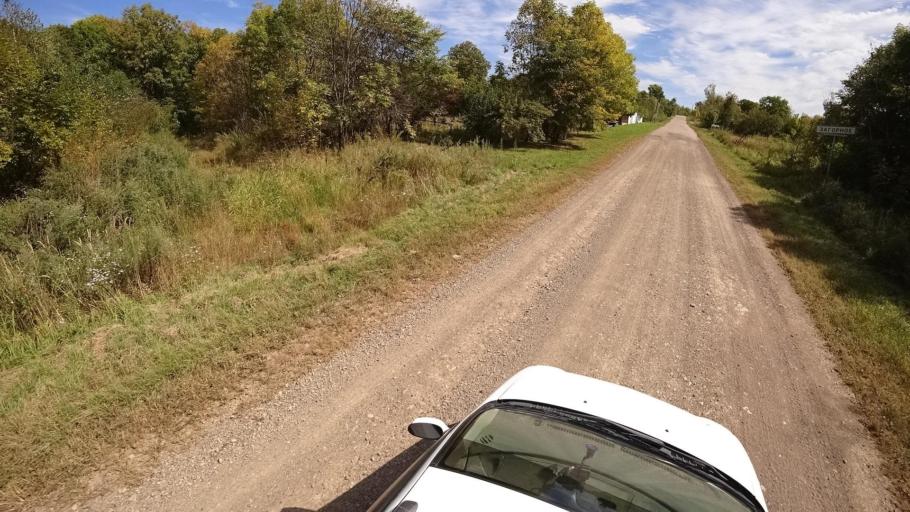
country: RU
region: Primorskiy
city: Yakovlevka
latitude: 44.6583
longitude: 133.7355
